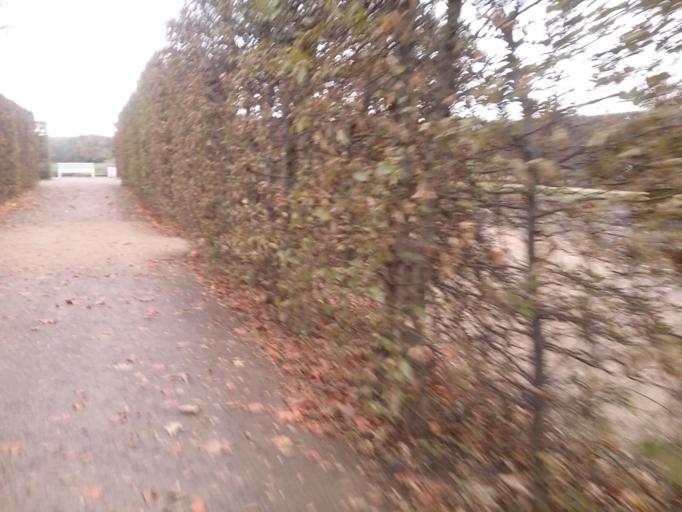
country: DE
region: Saxony
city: Heidenau
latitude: 51.0093
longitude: 13.8688
